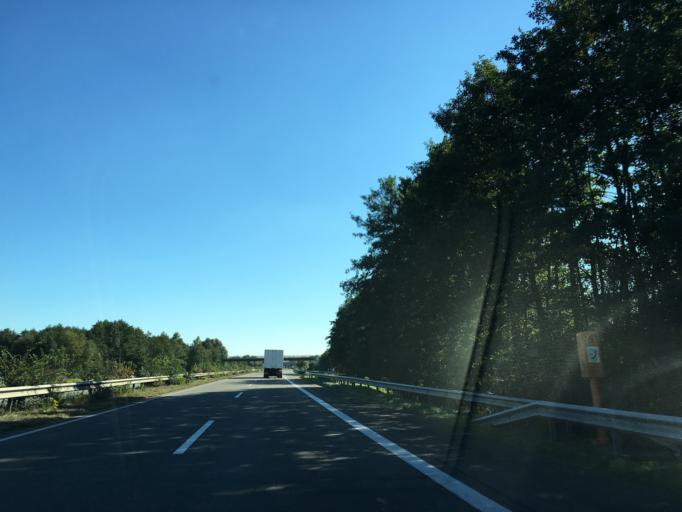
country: DE
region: Lower Saxony
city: Mechtersen
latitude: 53.3093
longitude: 10.3288
